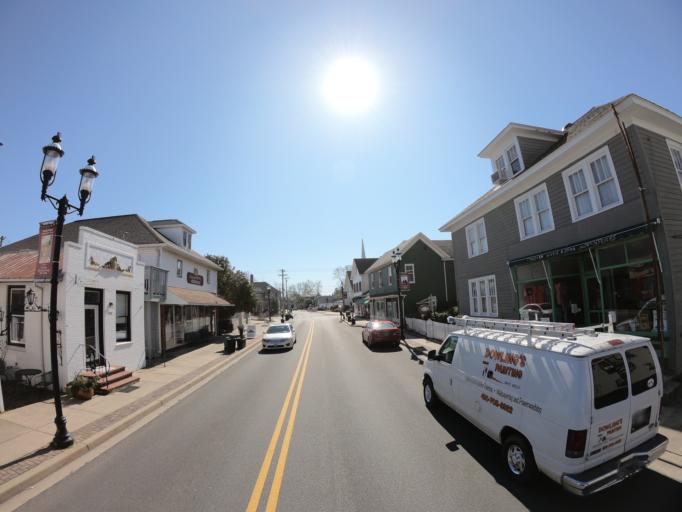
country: US
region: Maryland
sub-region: Kent County
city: Rock Hall
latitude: 39.1371
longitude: -76.2348
